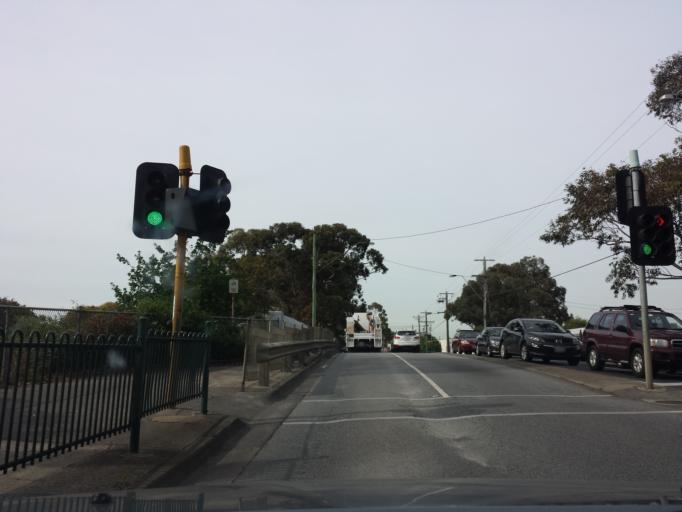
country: AU
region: Victoria
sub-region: Monash
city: Ashwood
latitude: -37.8750
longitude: 145.1292
